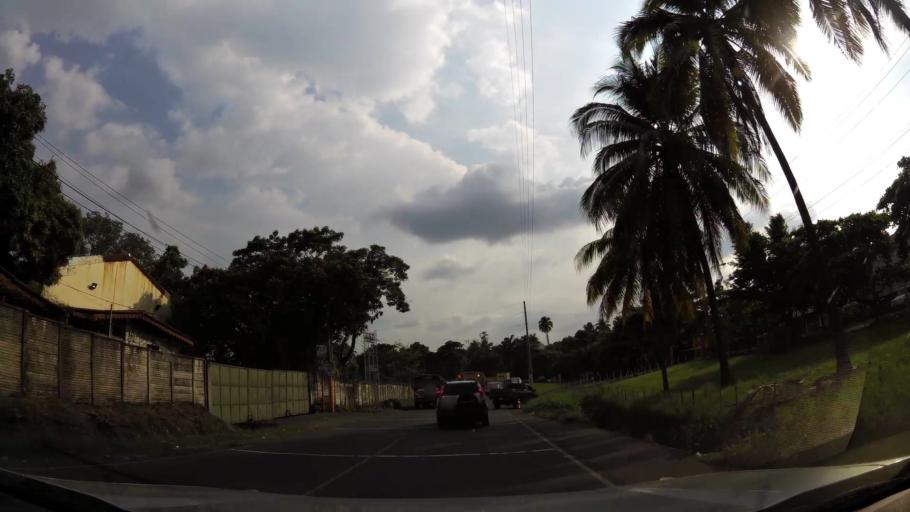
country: GT
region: Escuintla
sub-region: Municipio de Escuintla
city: Escuintla
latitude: 14.3070
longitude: -90.7928
